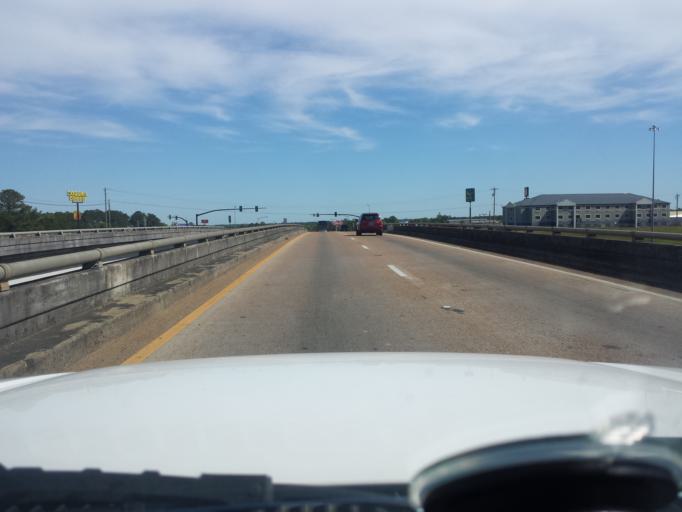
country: US
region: Mississippi
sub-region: Rankin County
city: Pearl
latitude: 32.2711
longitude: -90.0734
